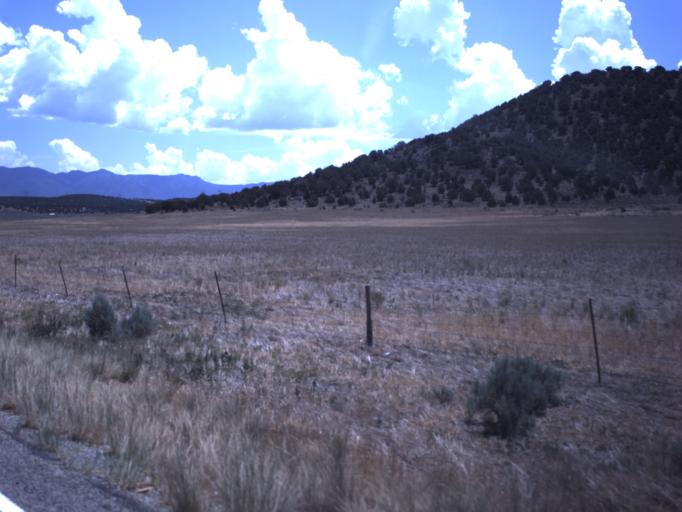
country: US
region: Utah
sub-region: Juab County
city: Nephi
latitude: 39.6970
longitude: -111.9814
